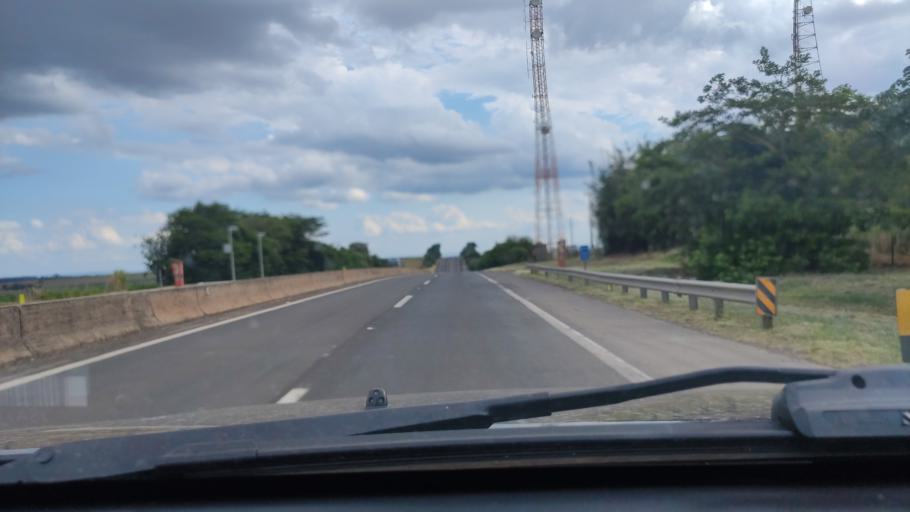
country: BR
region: Sao Paulo
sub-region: Santa Cruz Do Rio Pardo
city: Santa Cruz do Rio Pardo
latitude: -22.8233
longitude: -49.5496
